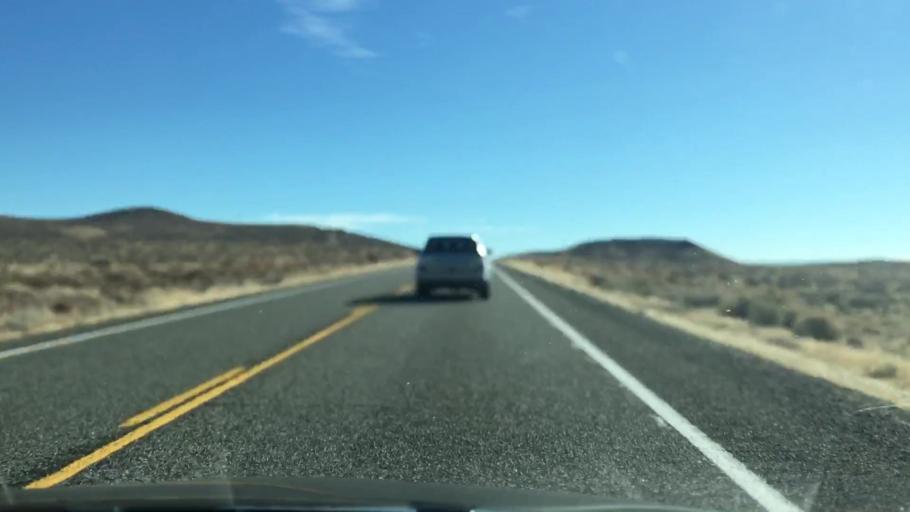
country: US
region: Nevada
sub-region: Lyon County
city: Silver Springs
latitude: 39.2323
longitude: -119.2311
